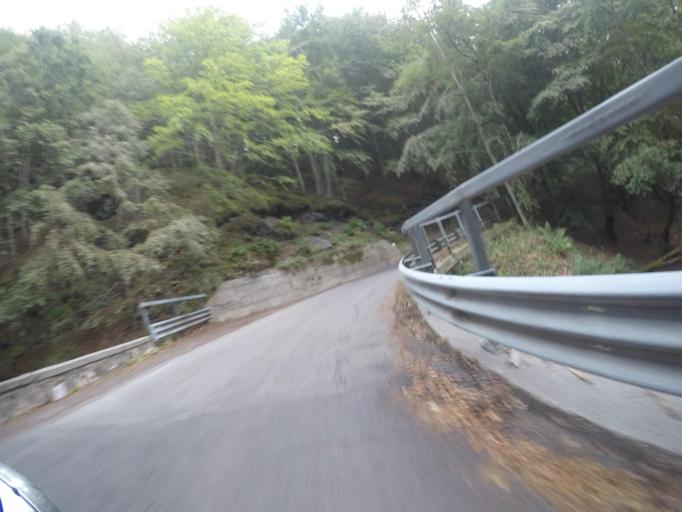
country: IT
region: Tuscany
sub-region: Provincia di Massa-Carrara
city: Carrara
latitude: 44.1157
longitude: 10.1222
